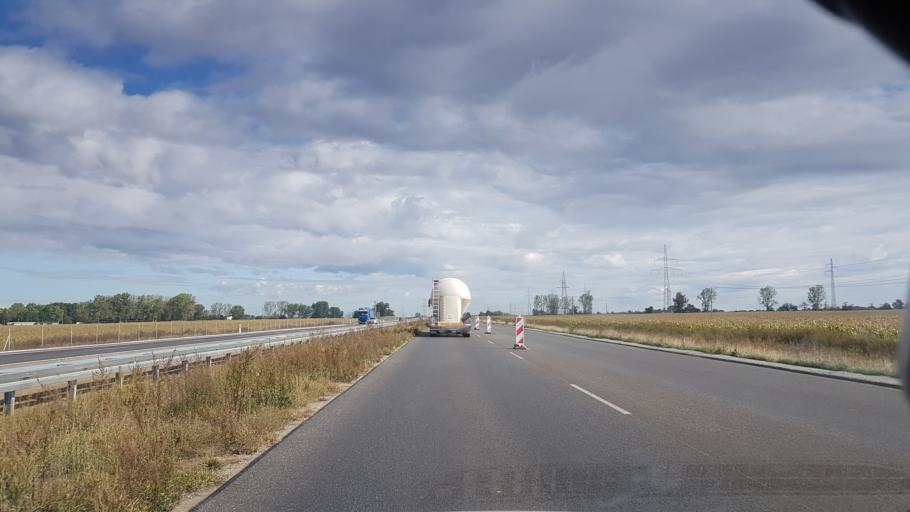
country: PL
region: Greater Poland Voivodeship
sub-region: Powiat poznanski
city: Steszew
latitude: 52.3219
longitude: 16.7169
